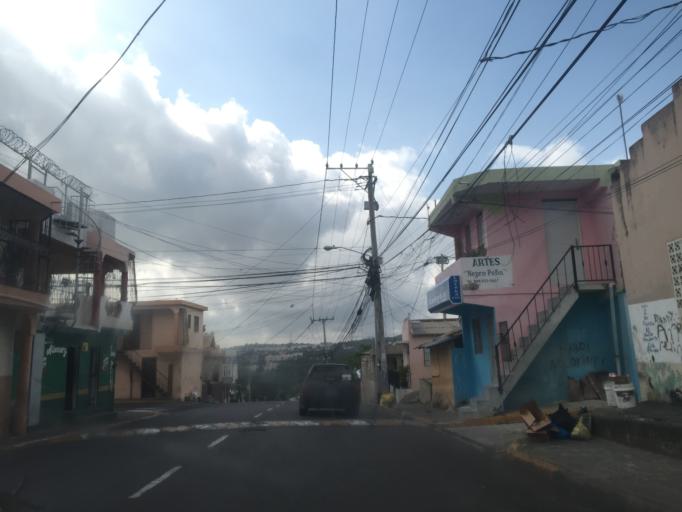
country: DO
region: Santiago
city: Santiago de los Caballeros
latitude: 19.4246
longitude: -70.7159
